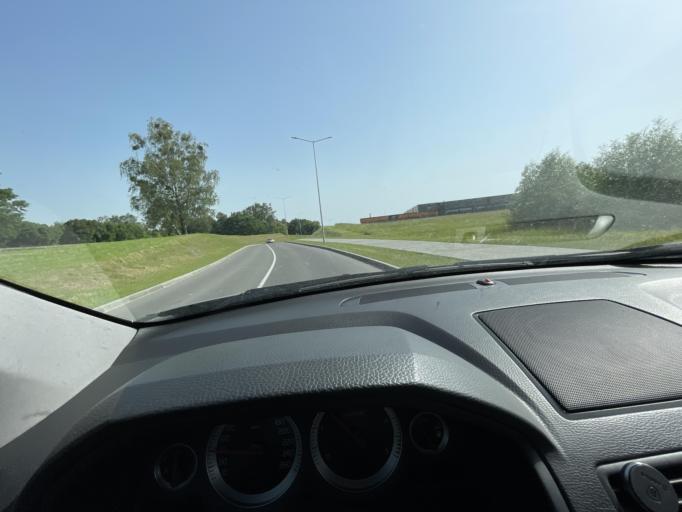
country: BY
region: Grodnenskaya
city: Hrodna
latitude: 53.6729
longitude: 23.8674
